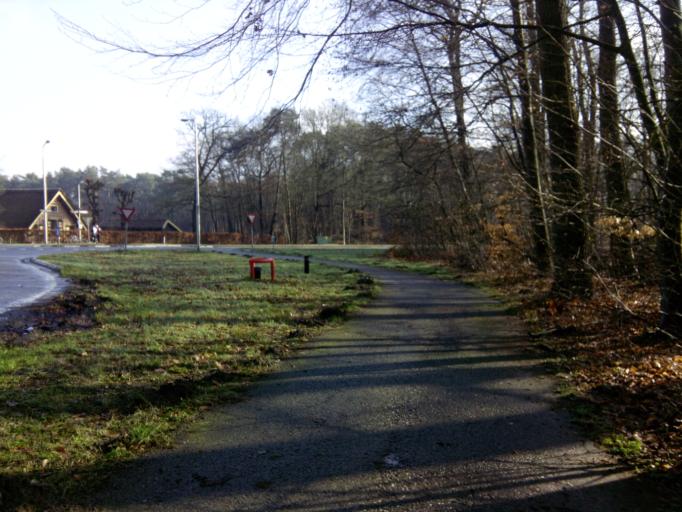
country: NL
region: Utrecht
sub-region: Gemeente Utrechtse Heuvelrug
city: Maarsbergen
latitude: 52.0474
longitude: 5.4040
